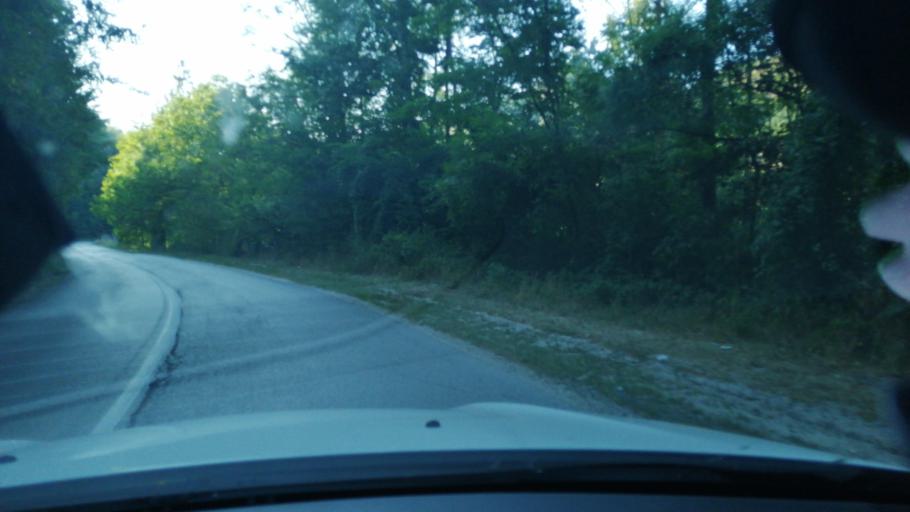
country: RS
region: Central Serbia
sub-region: Moravicki Okrug
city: Ivanjica
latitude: 43.6739
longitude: 20.2622
